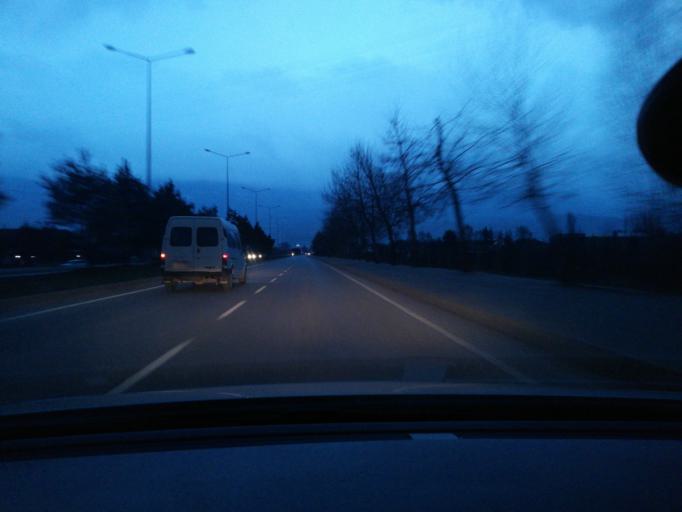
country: TR
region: Bolu
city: Bolu
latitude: 40.7098
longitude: 31.6163
